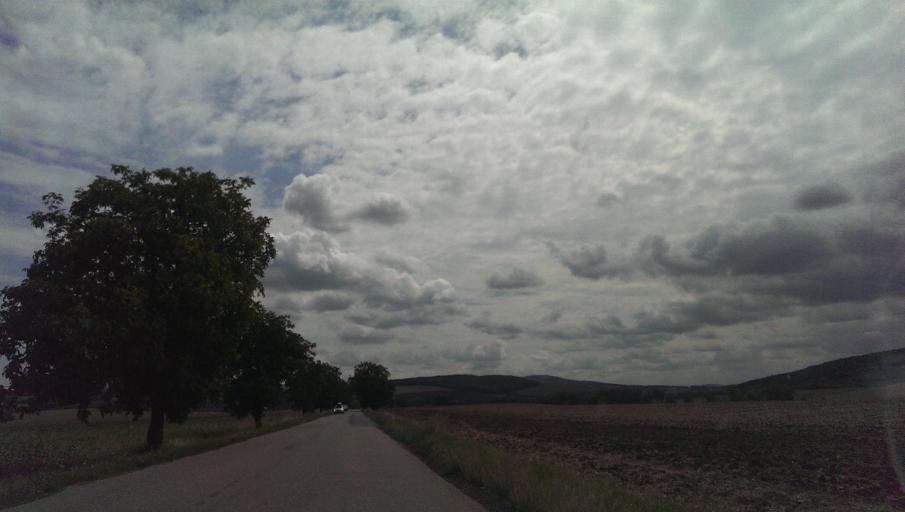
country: CZ
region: Zlin
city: Hluk
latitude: 48.9767
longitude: 17.5366
